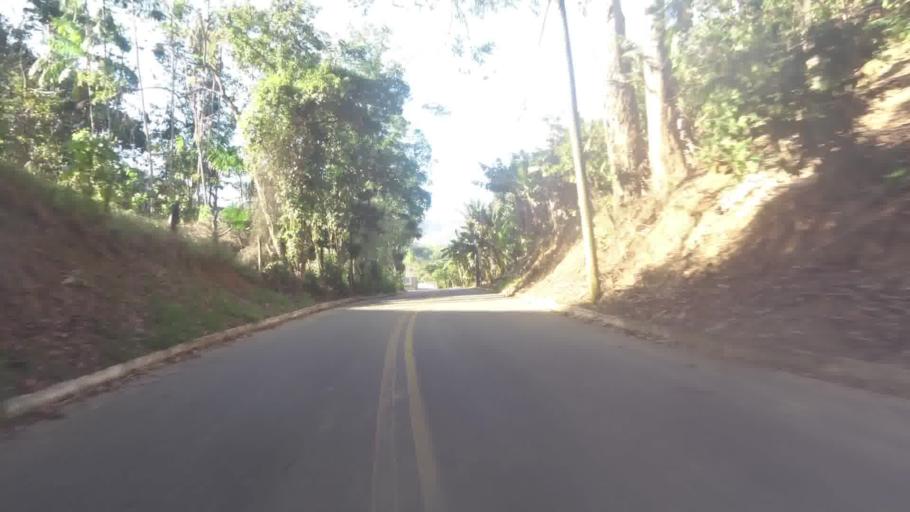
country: BR
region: Espirito Santo
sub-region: Iconha
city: Iconha
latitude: -20.7377
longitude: -40.7840
